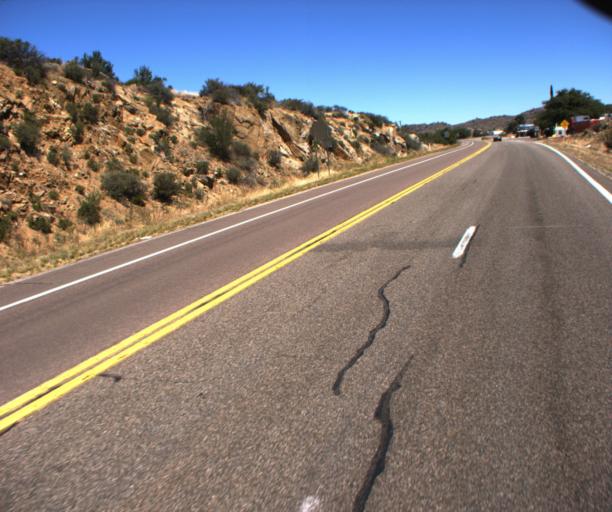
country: US
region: Arizona
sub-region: Yavapai County
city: Congress
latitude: 34.2103
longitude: -112.7554
